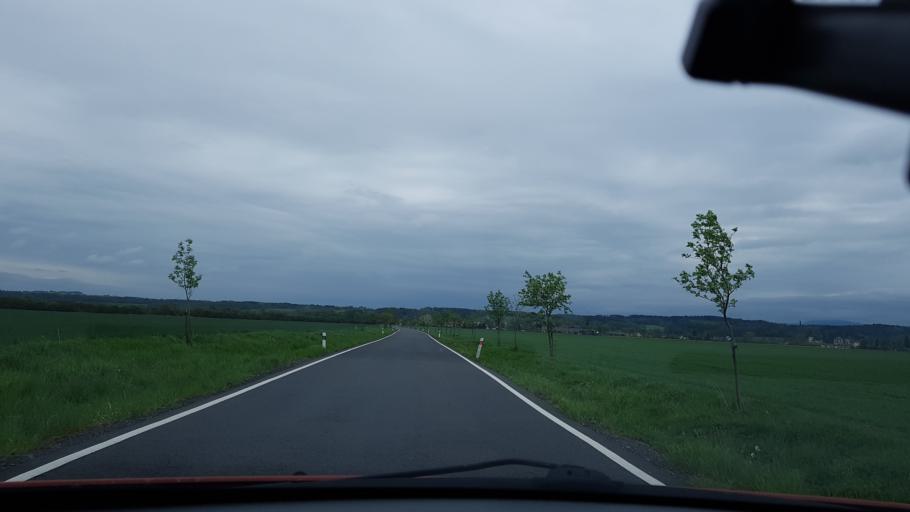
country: CZ
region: Olomoucky
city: Vidnava
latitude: 50.3792
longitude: 17.1627
